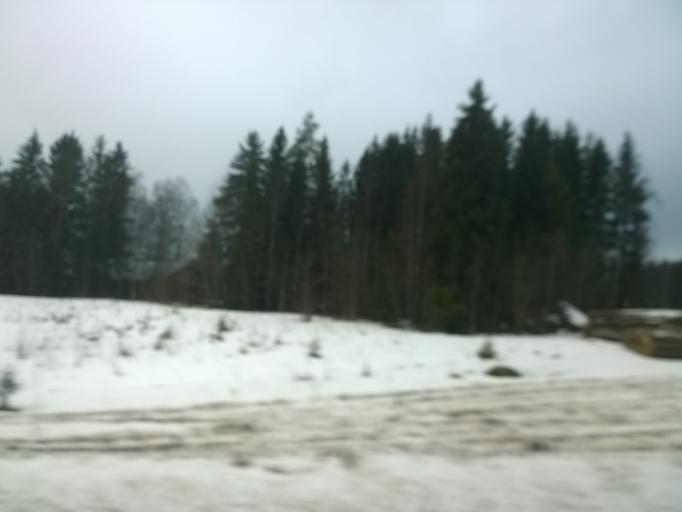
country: FI
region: Pirkanmaa
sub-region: Tampere
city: Lempaeaelae
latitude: 61.3738
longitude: 23.7875
